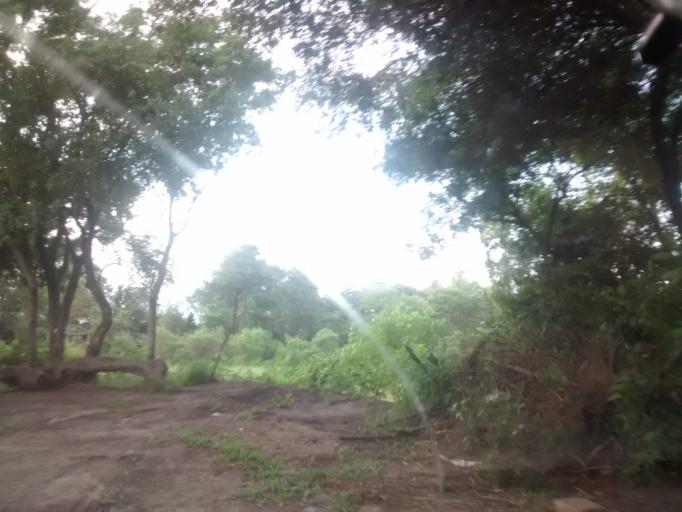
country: AR
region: Chaco
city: Fontana
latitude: -27.4204
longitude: -59.0026
